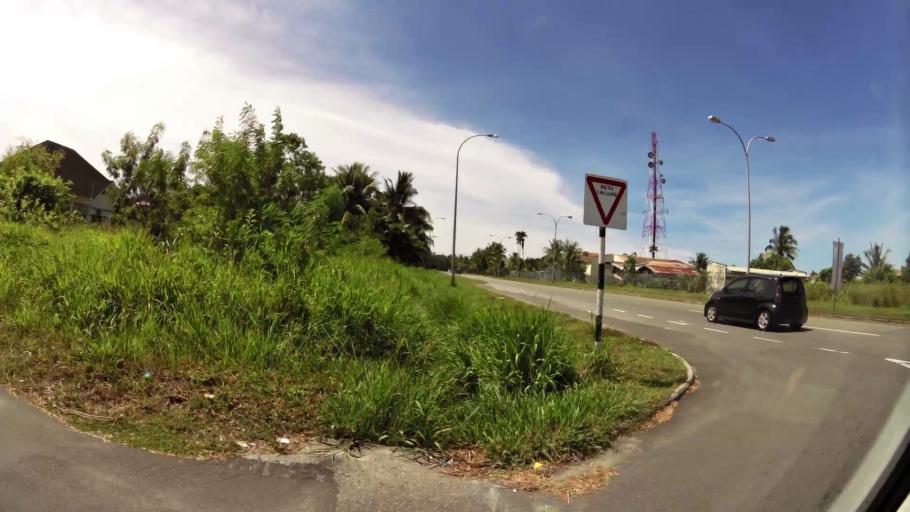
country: BN
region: Belait
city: Kuala Belait
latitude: 4.5896
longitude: 114.2309
